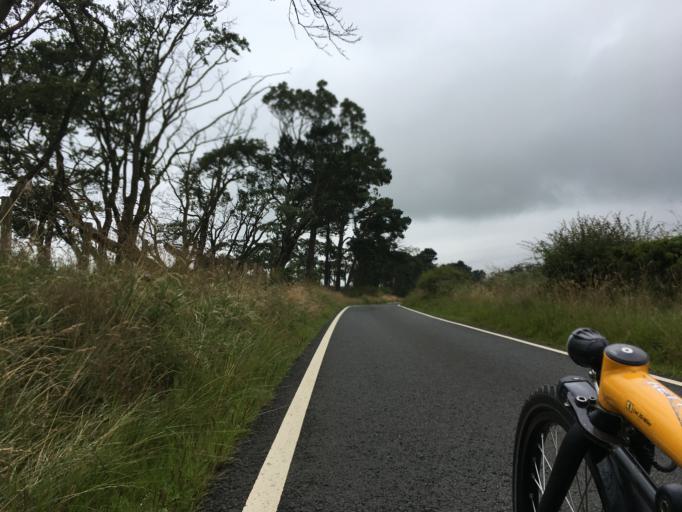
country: GB
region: Scotland
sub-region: West Lothian
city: West Calder
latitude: 55.8453
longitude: -3.5306
